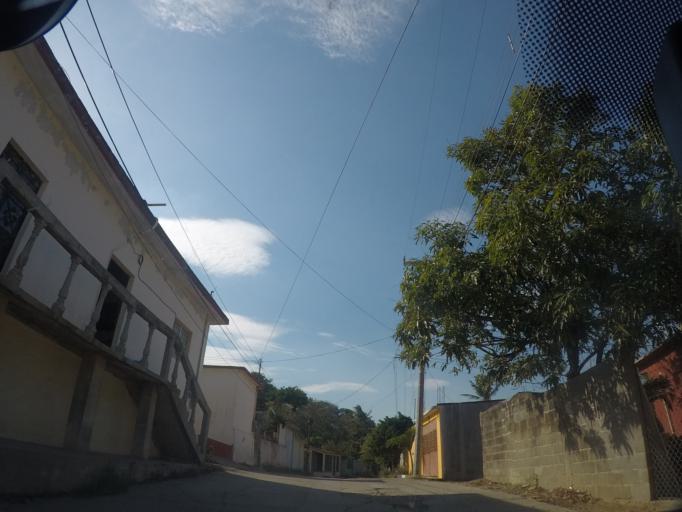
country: MX
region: Oaxaca
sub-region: Salina Cruz
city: Salina Cruz
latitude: 16.1963
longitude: -95.2037
